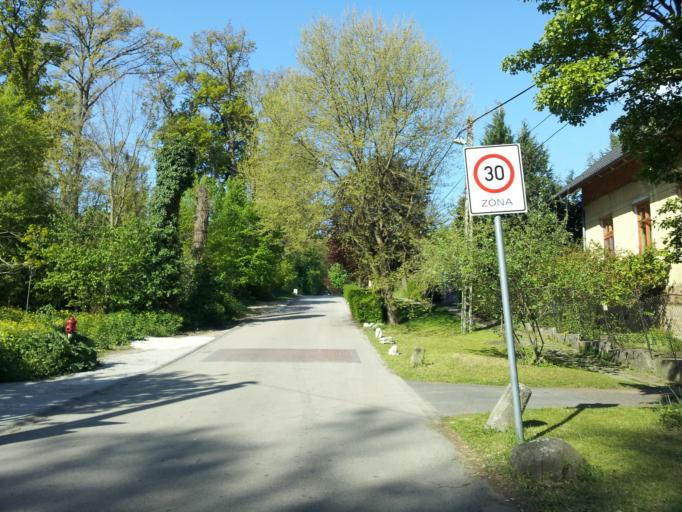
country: HU
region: Pest
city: Budakeszi
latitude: 47.5450
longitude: 18.9523
